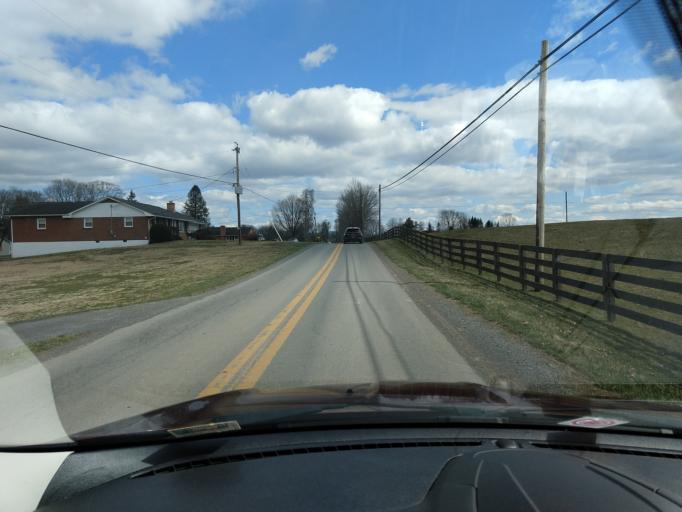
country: US
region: West Virginia
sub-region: Greenbrier County
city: Lewisburg
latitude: 37.8103
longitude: -80.4753
